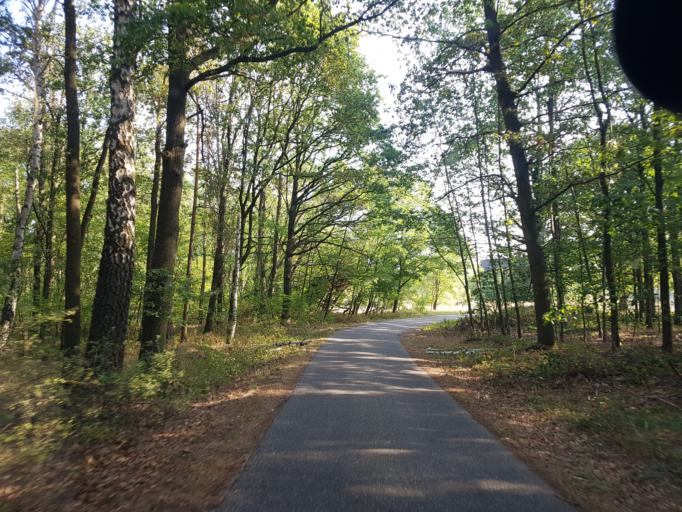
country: DE
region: Brandenburg
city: Sonnewalde
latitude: 51.6826
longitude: 13.6924
